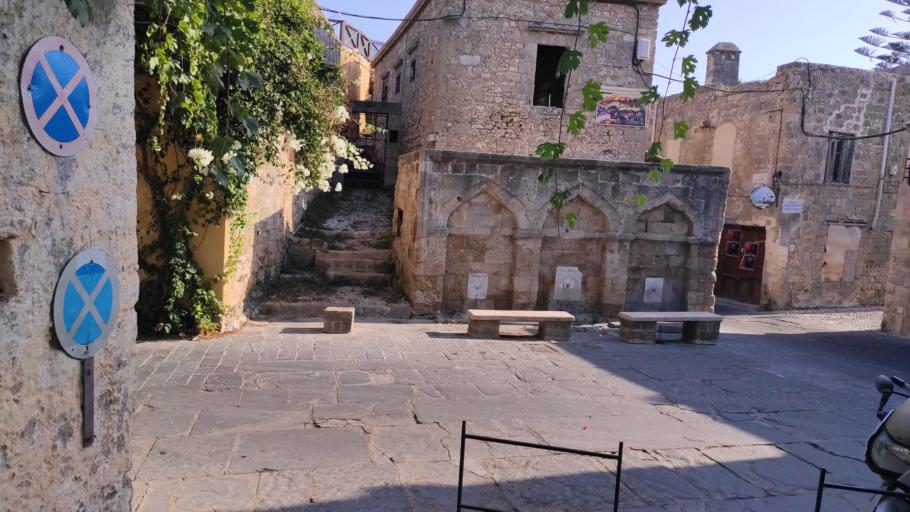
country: GR
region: South Aegean
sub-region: Nomos Dodekanisou
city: Rodos
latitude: 36.4409
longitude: 28.2280
